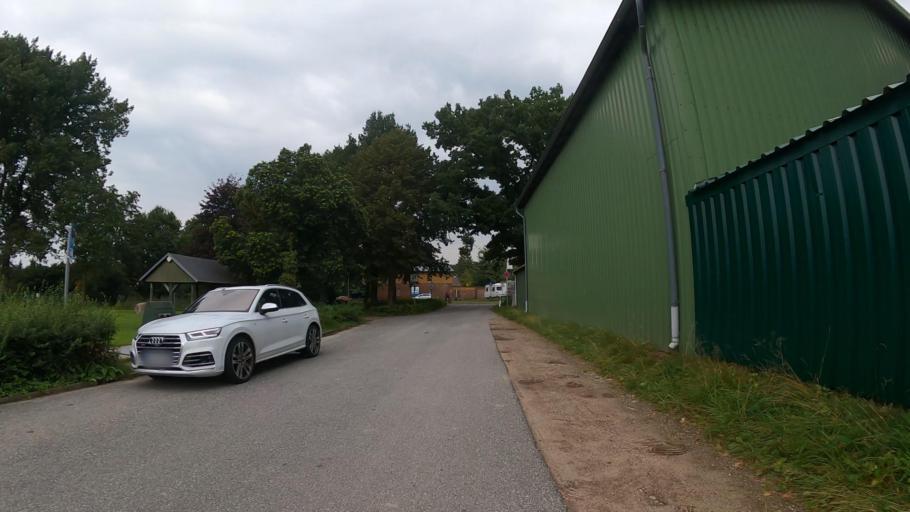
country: DE
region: Schleswig-Holstein
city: Prisdorf
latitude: 53.6785
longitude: 9.7567
